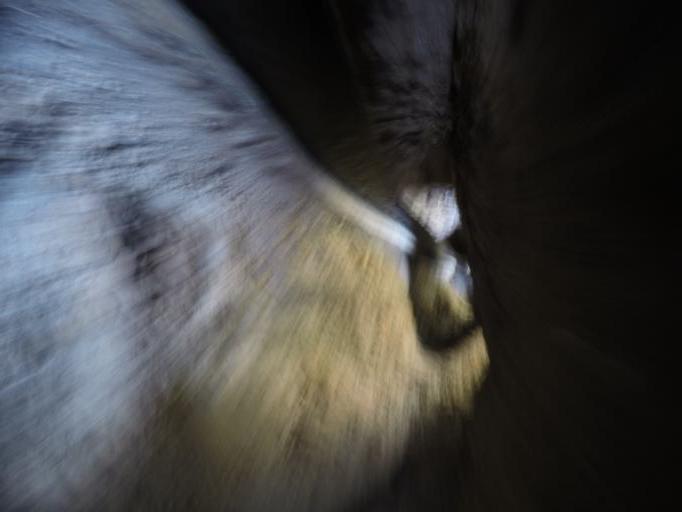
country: PT
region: Madeira
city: Camara de Lobos
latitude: 32.6621
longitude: -16.9592
